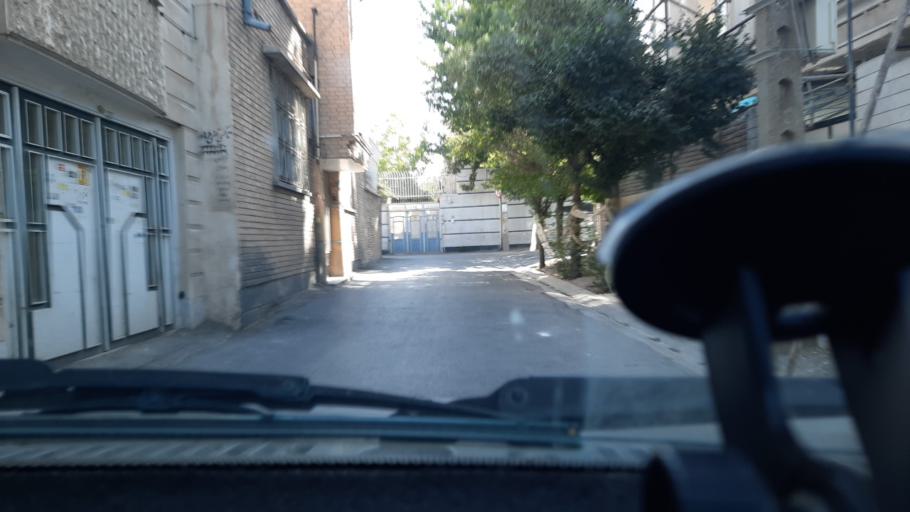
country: IR
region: Markazi
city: Arak
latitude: 34.0830
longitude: 49.6924
